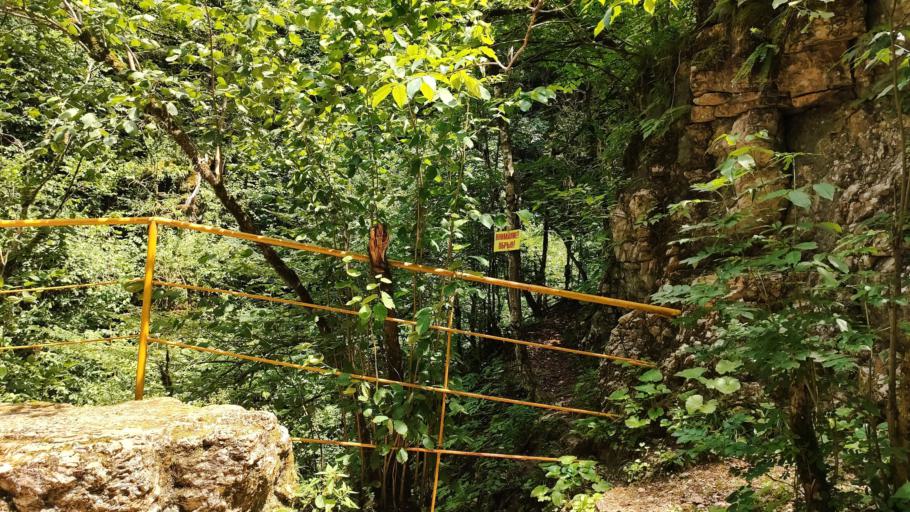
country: RU
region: Krasnodarskiy
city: Neftegorsk
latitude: 44.2080
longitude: 39.9100
